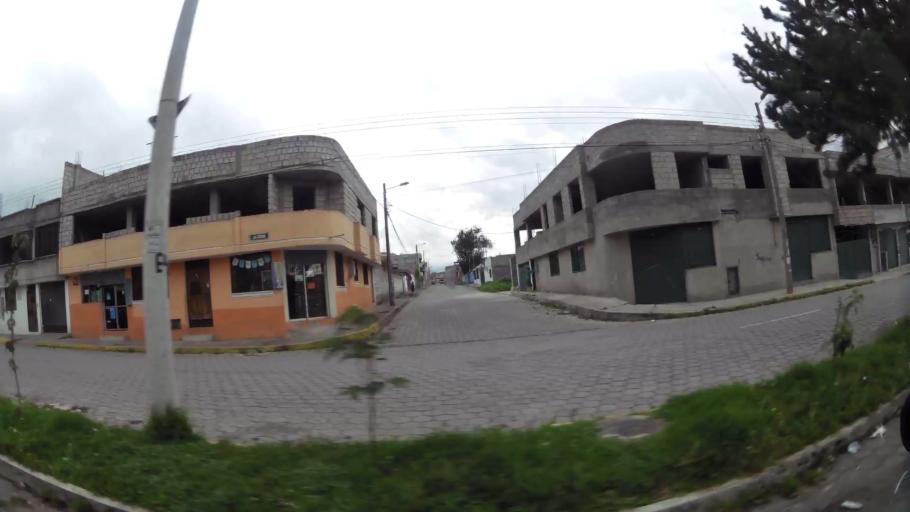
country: EC
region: Pichincha
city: Quito
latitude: -0.3133
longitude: -78.5371
